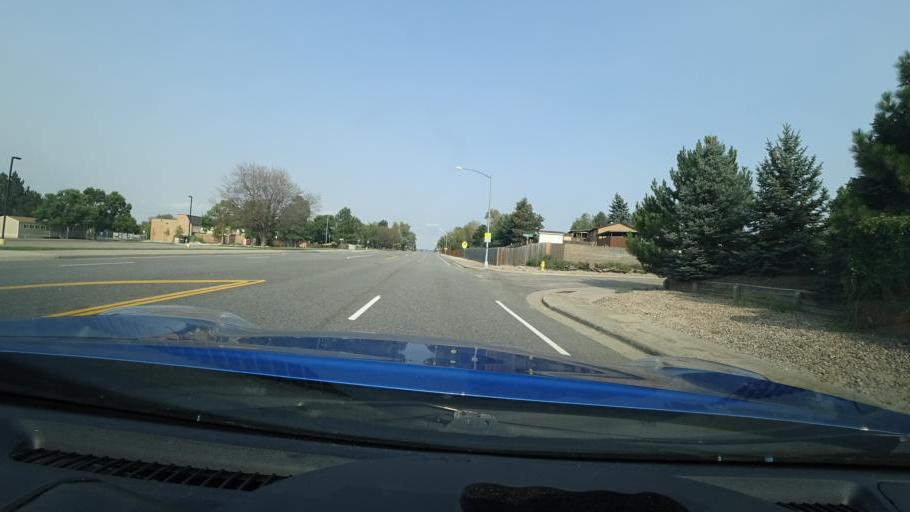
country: US
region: Colorado
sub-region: Adams County
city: Aurora
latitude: 39.6675
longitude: -104.8052
